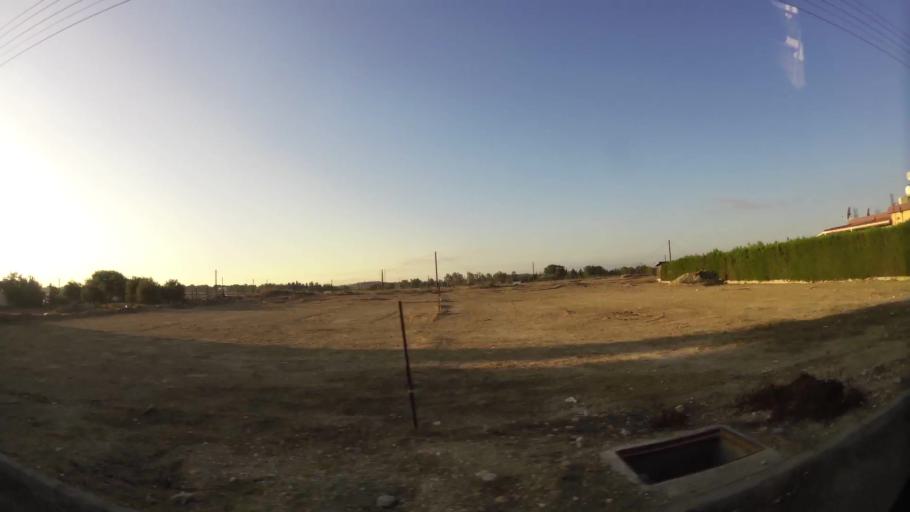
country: CY
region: Lefkosia
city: Nicosia
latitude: 35.1902
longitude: 33.3152
